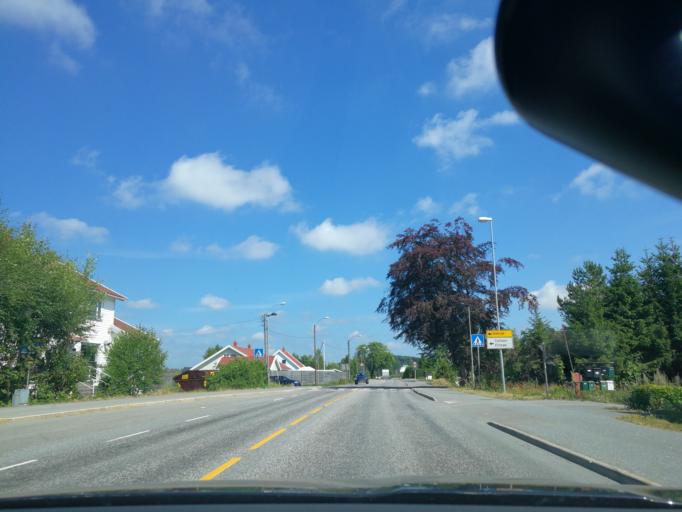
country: NO
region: Vestfold
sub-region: Sandefjord
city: Sandefjord
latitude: 59.1627
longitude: 10.2020
